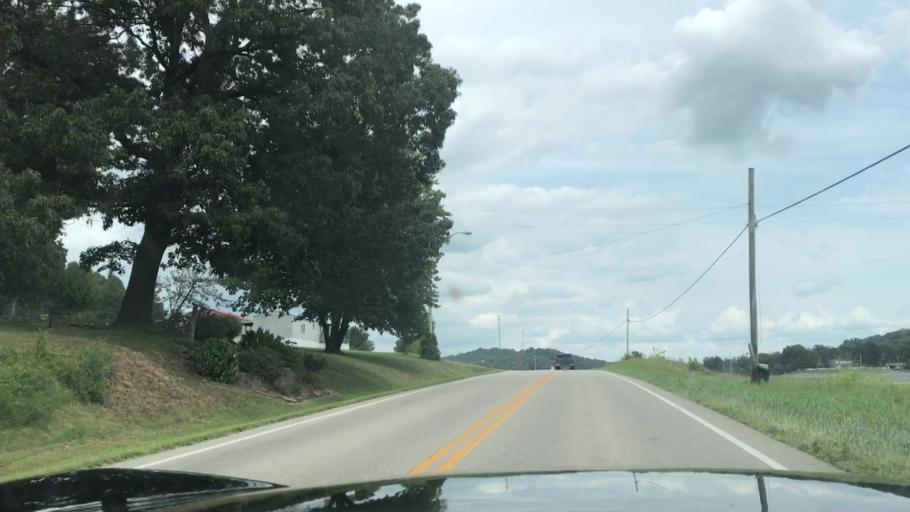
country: US
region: Kentucky
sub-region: Butler County
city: Morgantown
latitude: 37.2116
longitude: -86.7157
